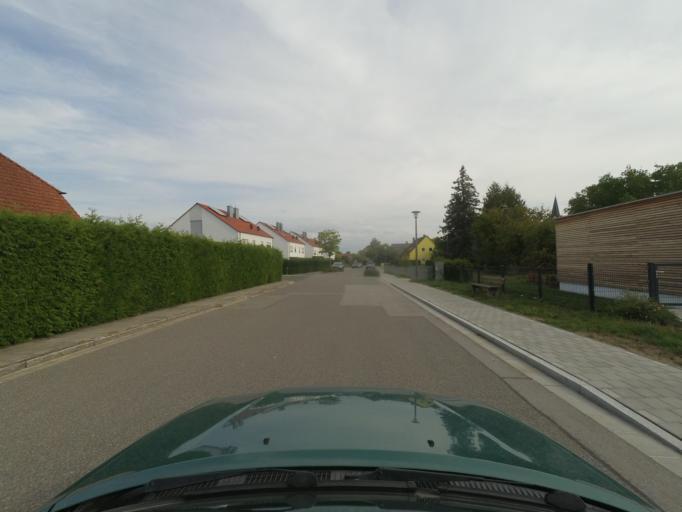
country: DE
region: Bavaria
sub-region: Upper Palatinate
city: Freystadt
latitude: 49.2018
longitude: 11.3289
